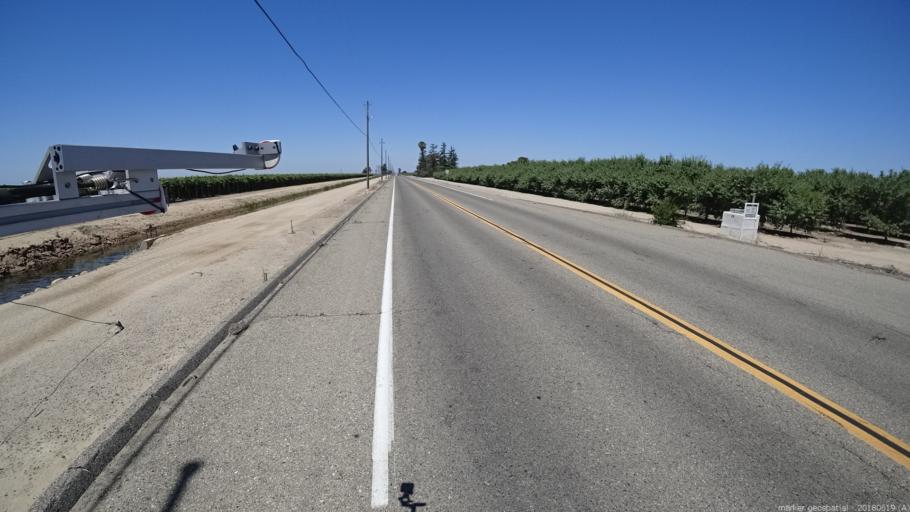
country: US
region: California
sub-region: Fresno County
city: Biola
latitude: 36.8513
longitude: -120.0741
